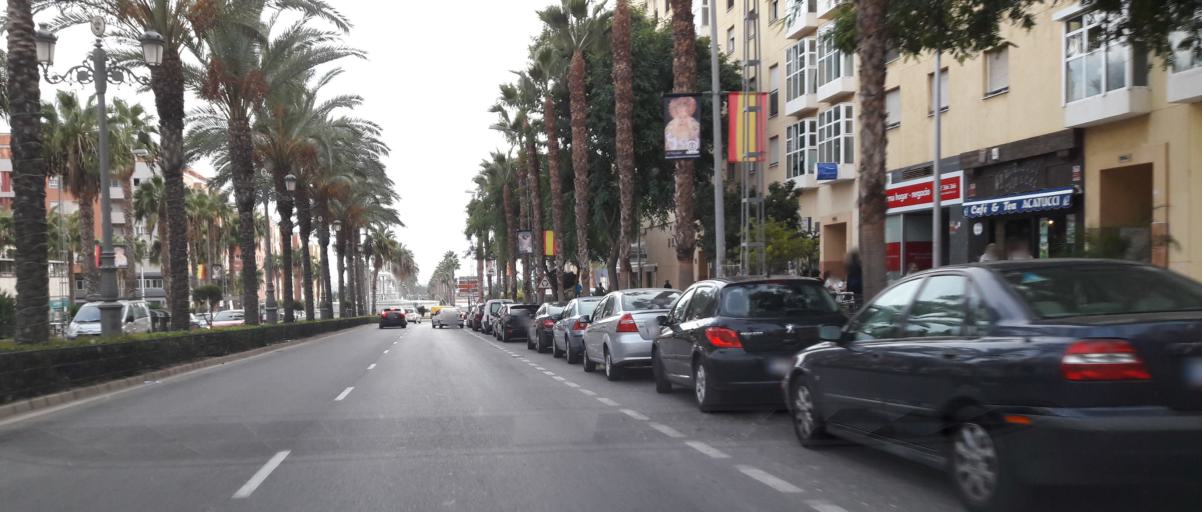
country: ES
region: Andalusia
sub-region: Provincia de Almeria
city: Aguadulce
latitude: 36.8045
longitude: -2.5994
